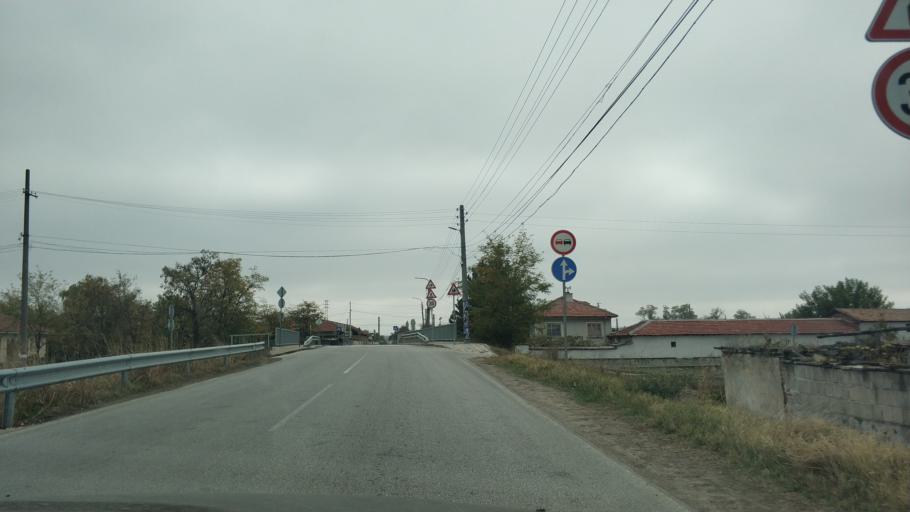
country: BG
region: Plovdiv
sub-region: Obshtina Kaloyanovo
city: Kaloyanovo
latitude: 42.3695
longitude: 24.7234
